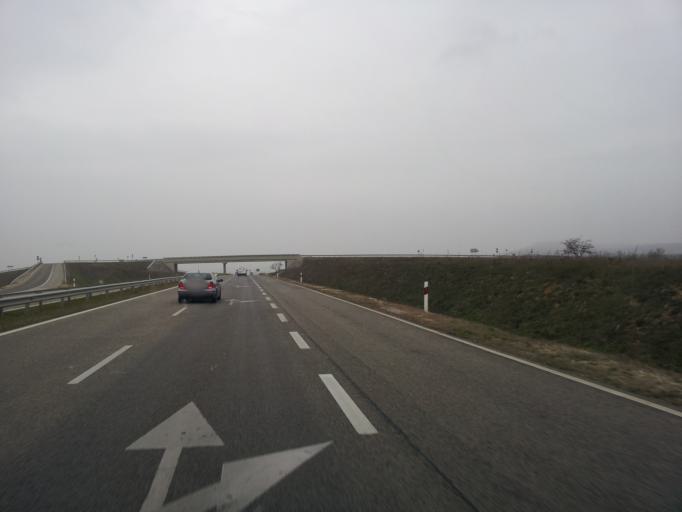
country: HU
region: Veszprem
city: Herend
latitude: 47.1179
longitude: 17.8057
